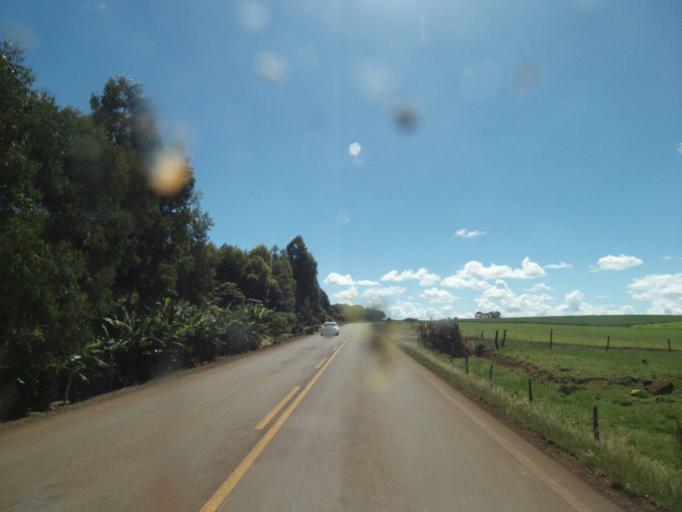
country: BR
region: Parana
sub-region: Pinhao
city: Pinhao
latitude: -25.8132
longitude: -52.0639
